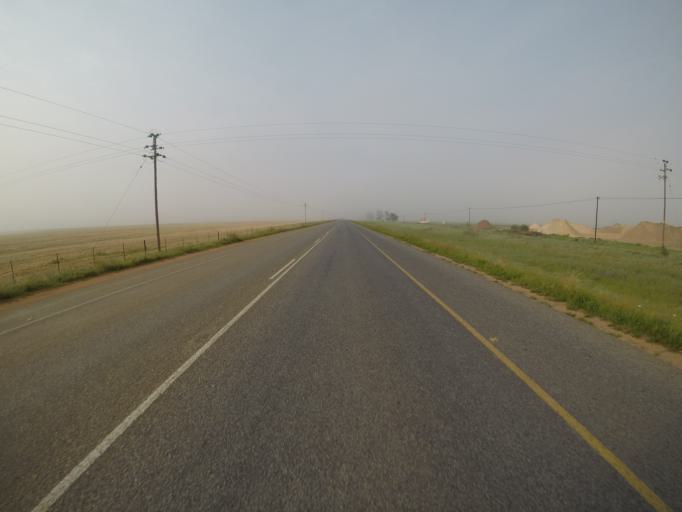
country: ZA
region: Western Cape
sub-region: City of Cape Town
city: Kraaifontein
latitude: -33.6662
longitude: 18.7076
